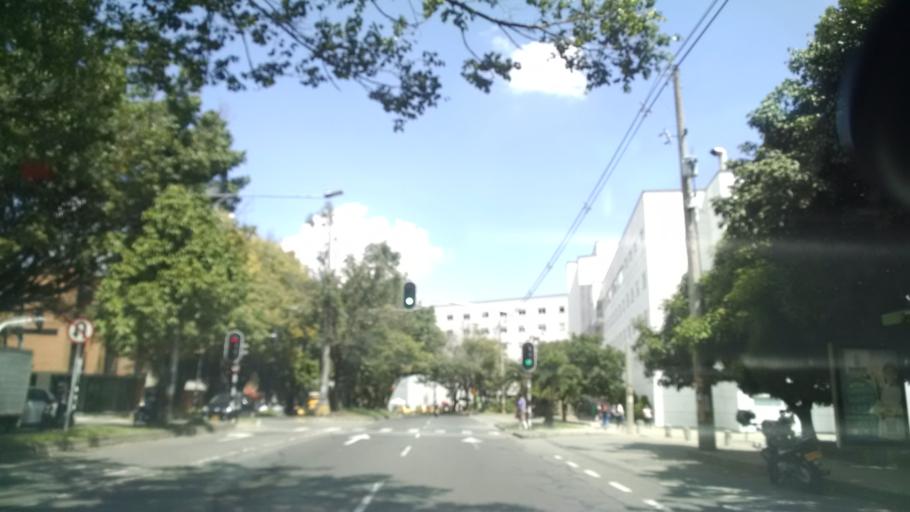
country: CO
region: Antioquia
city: Itagui
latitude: 6.2238
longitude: -75.5994
